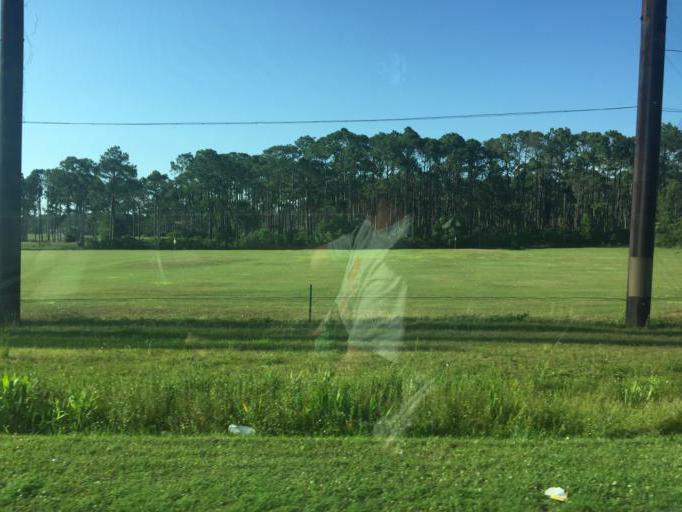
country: US
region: Florida
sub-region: Bay County
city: Panama City Beach
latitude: 30.2058
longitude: -85.8379
